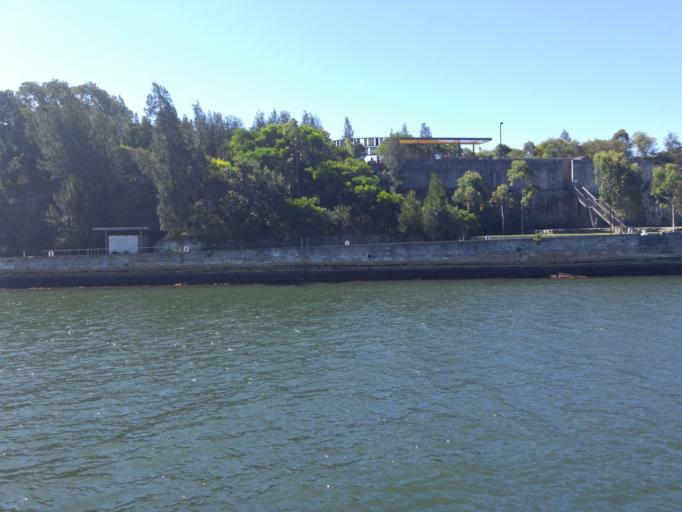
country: AU
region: New South Wales
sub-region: Leichhardt
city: Balmain East
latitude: -33.8537
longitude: 151.1893
